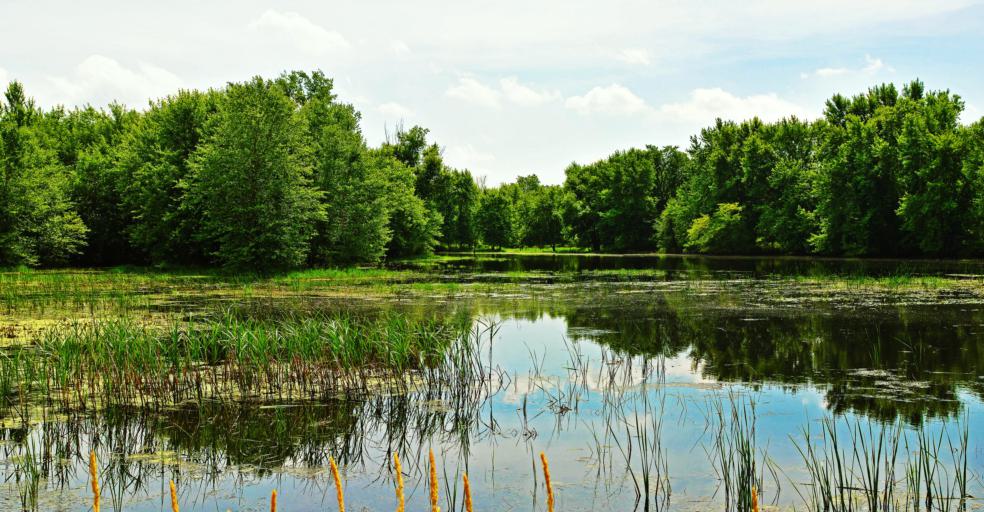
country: US
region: Wisconsin
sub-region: Pepin County
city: Durand
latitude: 44.7290
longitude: -91.8693
